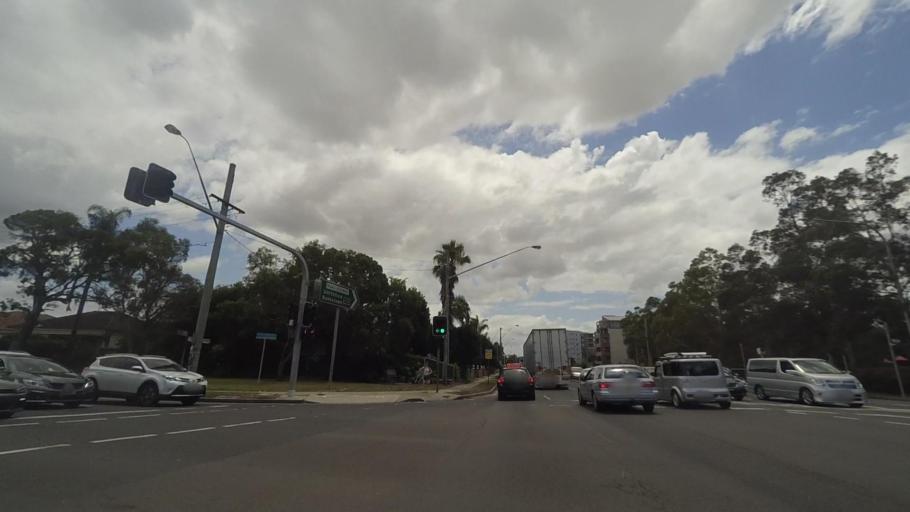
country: AU
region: New South Wales
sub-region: Fairfield
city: Liverpool
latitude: -33.9195
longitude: 150.9193
